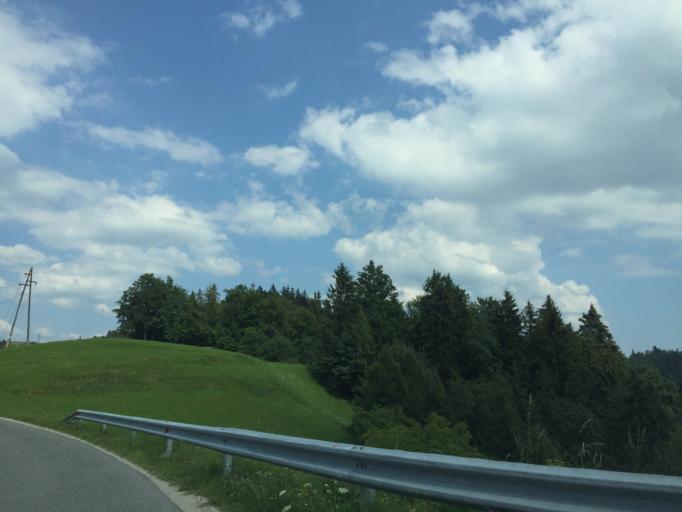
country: SI
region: Sostanj
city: Ravne
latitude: 46.4163
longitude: 15.1108
